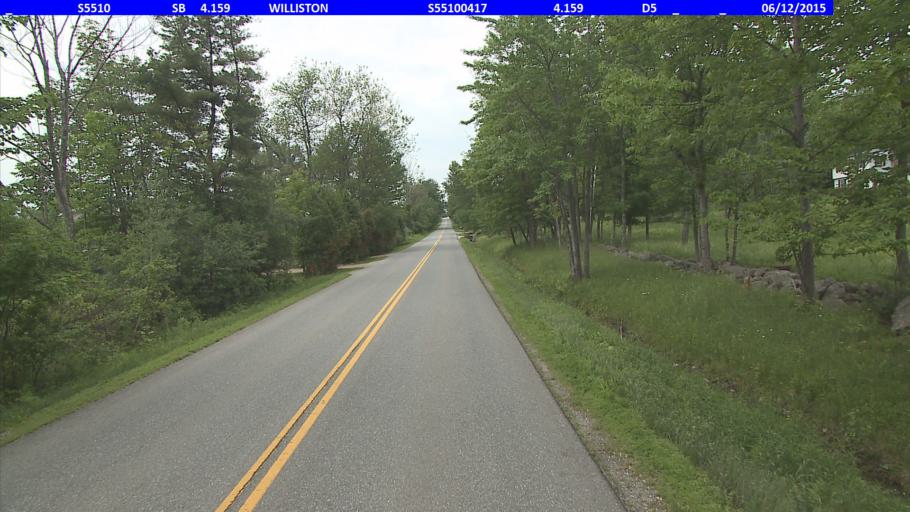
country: US
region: Vermont
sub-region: Chittenden County
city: Williston
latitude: 44.4288
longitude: -73.0750
